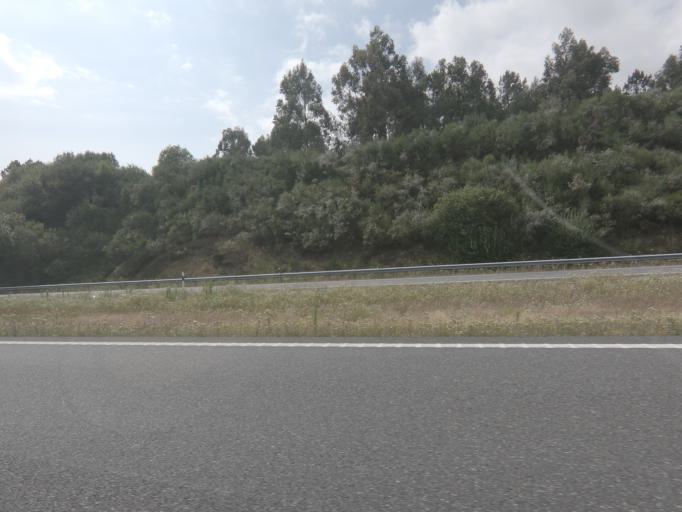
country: ES
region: Galicia
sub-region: Provincia de Ourense
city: Melon
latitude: 42.2137
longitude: -8.2603
